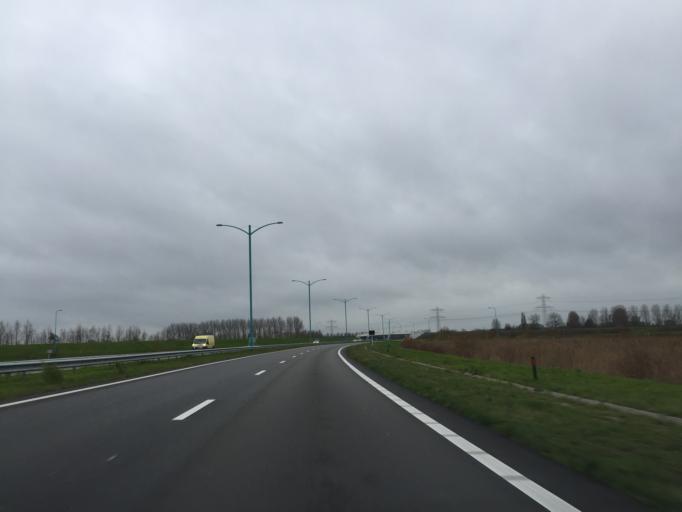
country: NL
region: Zeeland
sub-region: Gemeente Terneuzen
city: Terneuzen
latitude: 51.3278
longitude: 3.8003
